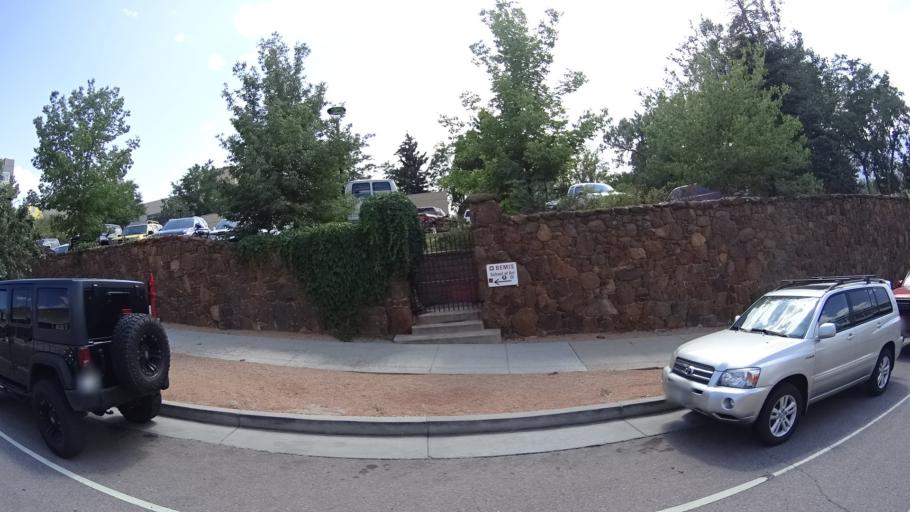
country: US
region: Colorado
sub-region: El Paso County
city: Colorado Springs
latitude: 38.8467
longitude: -104.8269
